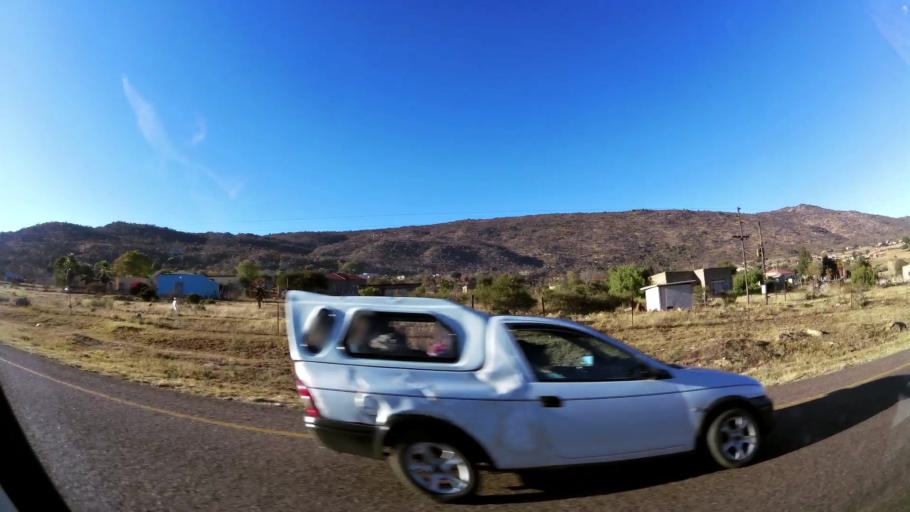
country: ZA
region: Limpopo
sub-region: Capricorn District Municipality
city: Mankoeng
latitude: -23.9399
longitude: 29.8266
